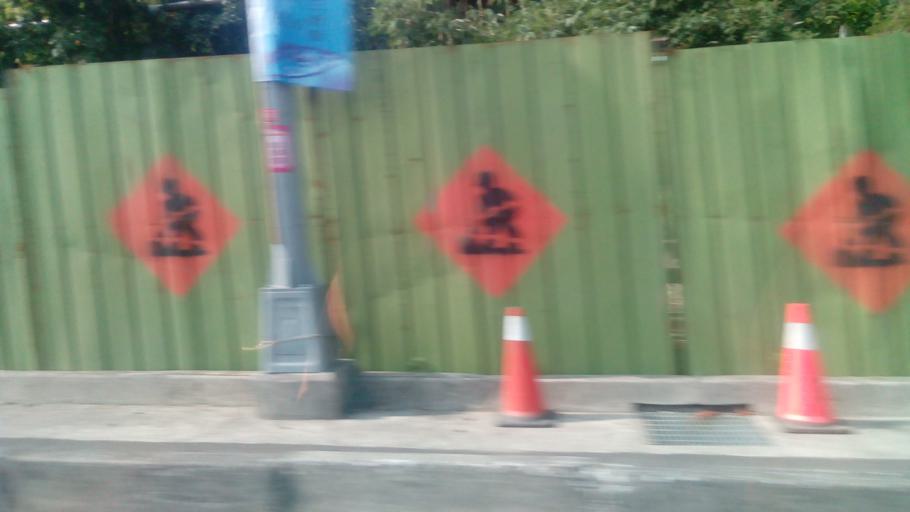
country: TW
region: Taiwan
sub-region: Yilan
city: Yilan
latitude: 24.5881
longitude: 121.8622
